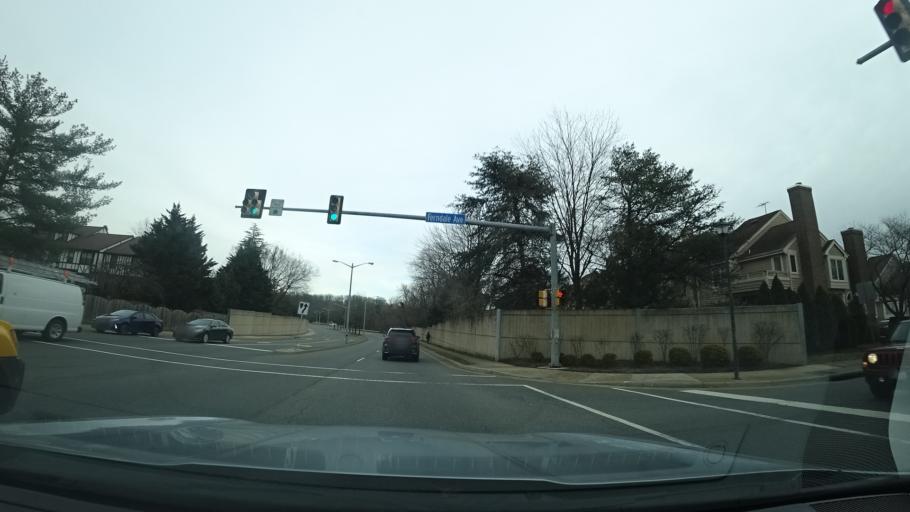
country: US
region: Virginia
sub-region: Fairfax County
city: Herndon
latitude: 38.9787
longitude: -77.3924
